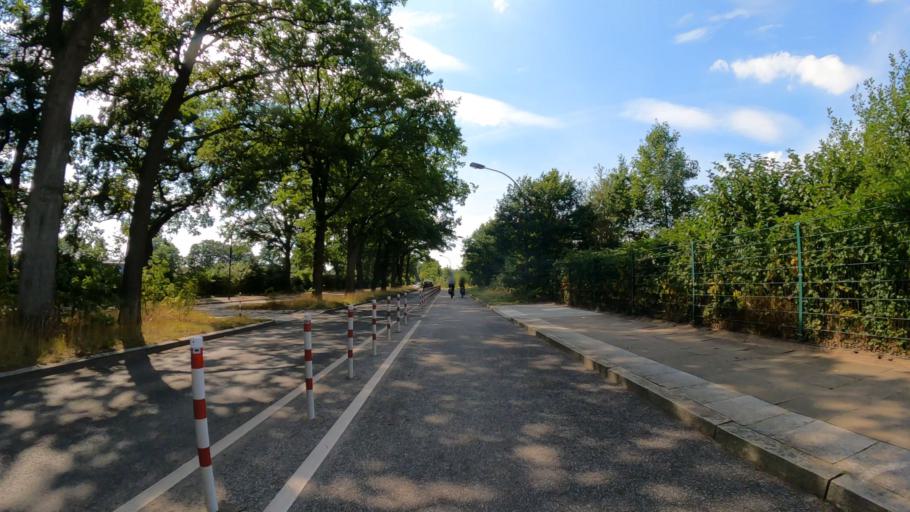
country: DE
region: Schleswig-Holstein
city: Norderstedt
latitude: 53.7238
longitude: 10.0169
